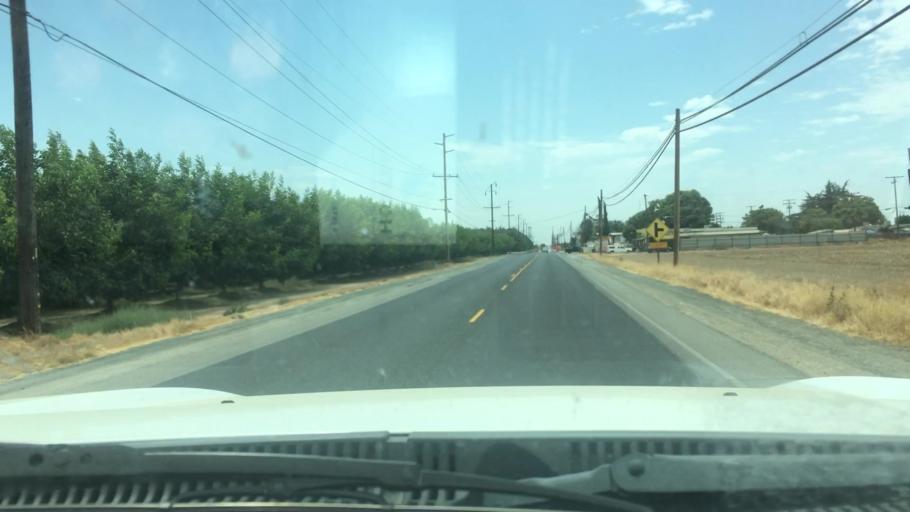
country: US
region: California
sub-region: Tulare County
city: Poplar-Cotton Center
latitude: 36.0658
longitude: -119.0980
